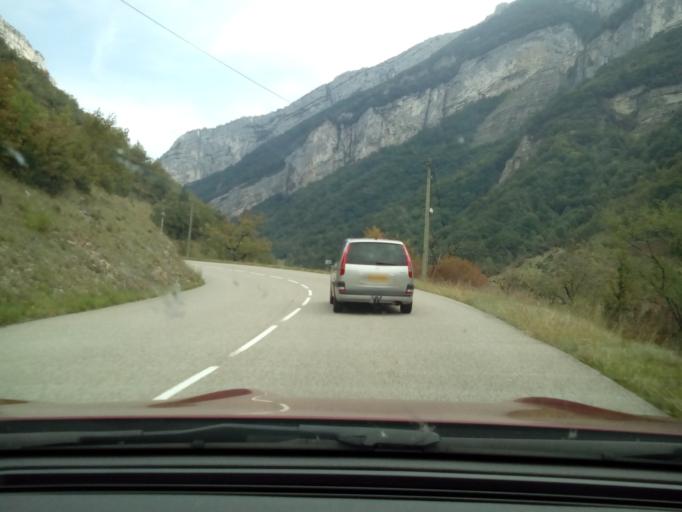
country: FR
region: Rhone-Alpes
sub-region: Departement de la Drome
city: Saint-Laurent-en-Royans
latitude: 45.0199
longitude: 5.3942
